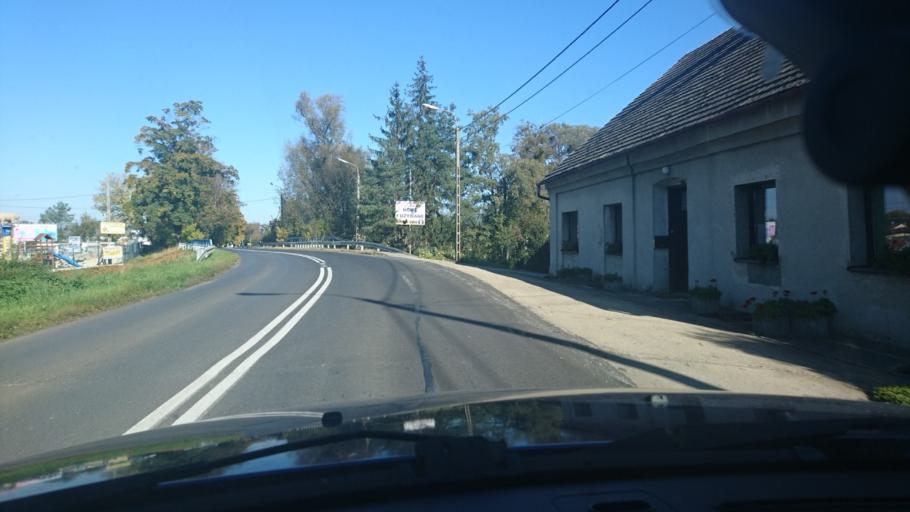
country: PL
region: Silesian Voivodeship
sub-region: Powiat bielski
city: Jasienica
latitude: 49.8173
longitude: 18.9185
